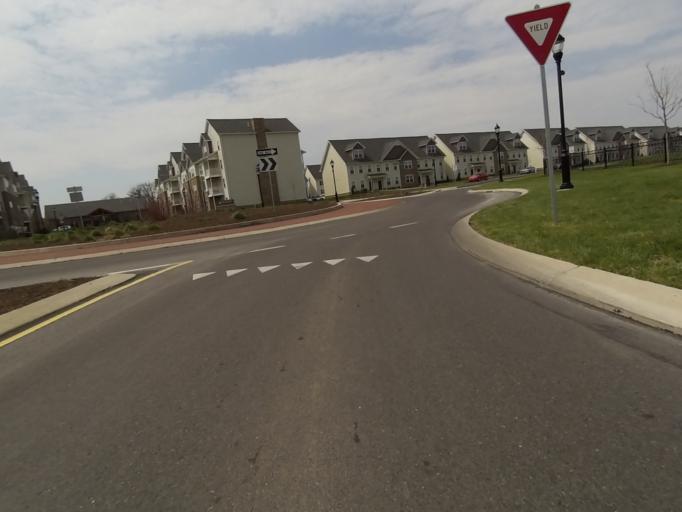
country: US
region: Pennsylvania
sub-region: Centre County
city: Park Forest Village
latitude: 40.7889
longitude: -77.8953
